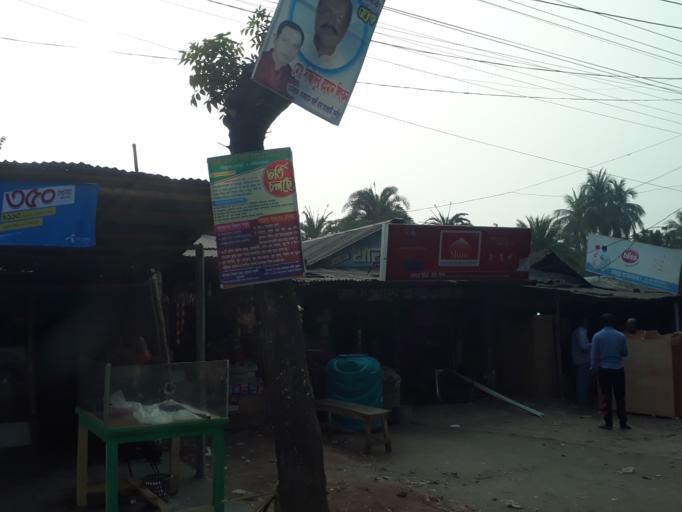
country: BD
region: Khulna
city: Bhatpara Abhaynagar
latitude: 22.9268
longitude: 89.4965
